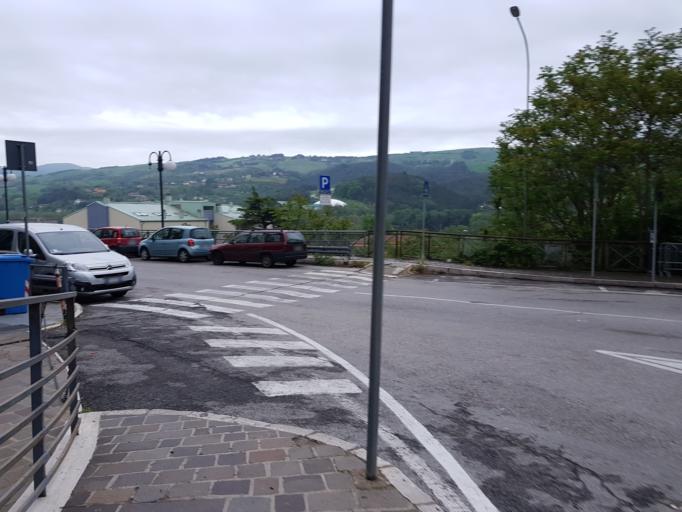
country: IT
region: Basilicate
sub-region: Provincia di Potenza
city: Potenza
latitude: 40.6302
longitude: 15.8051
